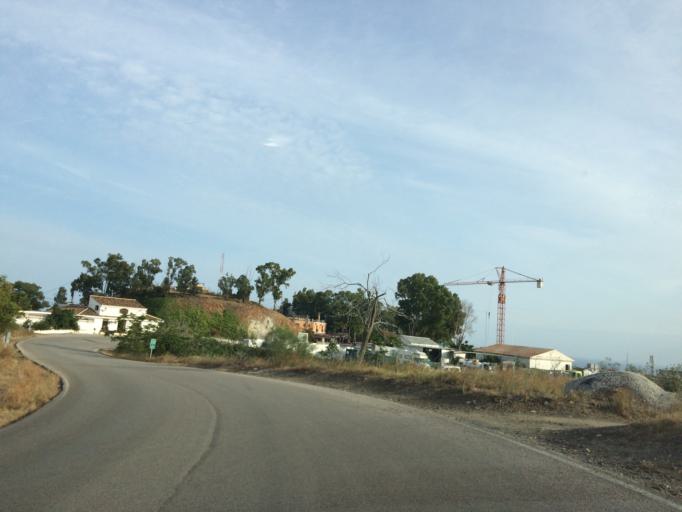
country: ES
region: Andalusia
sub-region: Provincia de Malaga
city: Malaga
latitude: 36.7500
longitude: -4.4080
